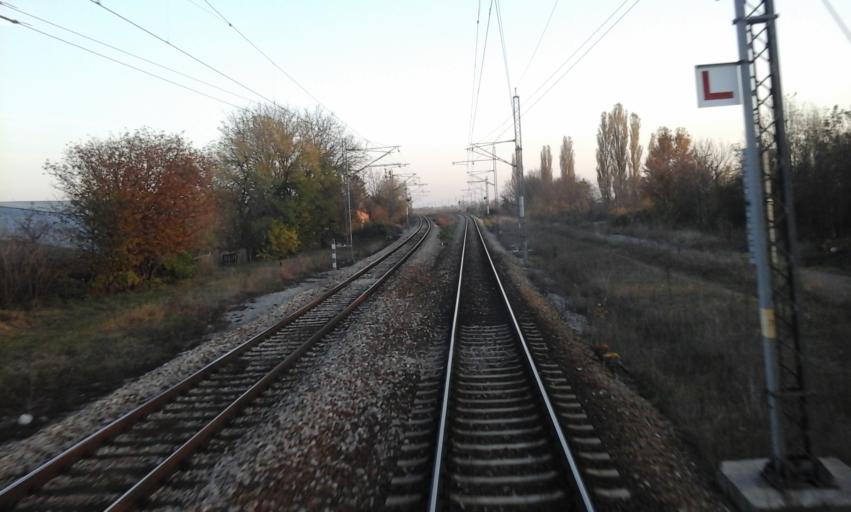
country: RS
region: Autonomna Pokrajina Vojvodina
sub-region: Sremski Okrug
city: Stara Pazova
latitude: 44.9826
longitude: 20.1403
